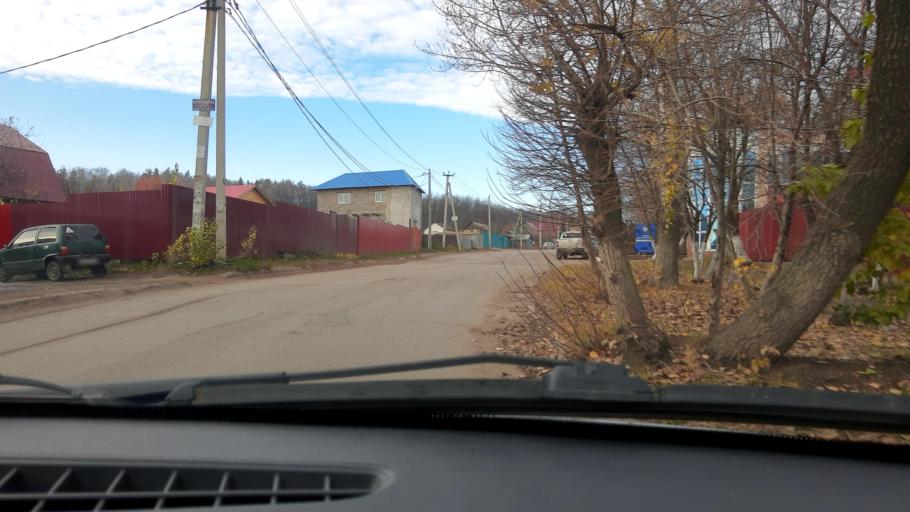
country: RU
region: Bashkortostan
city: Avdon
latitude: 54.6822
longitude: 55.7973
